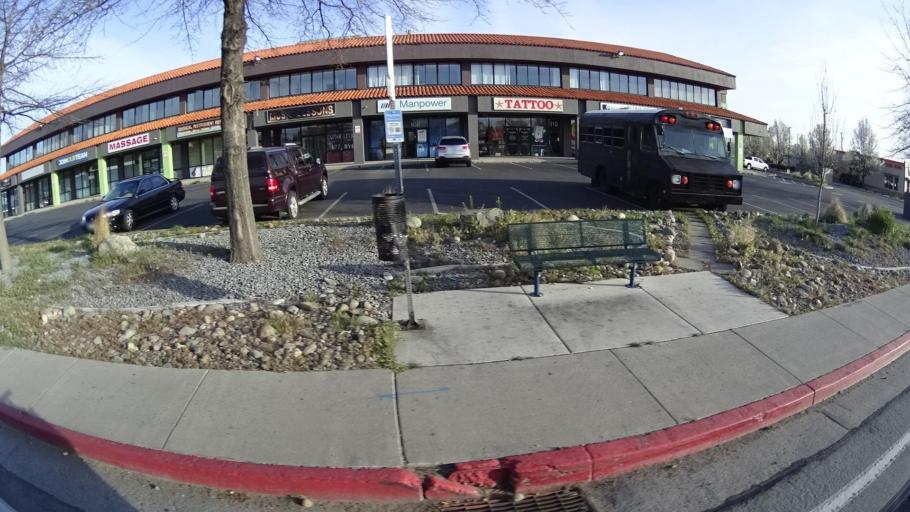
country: US
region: Nevada
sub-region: Washoe County
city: Reno
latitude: 39.5263
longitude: -119.8294
